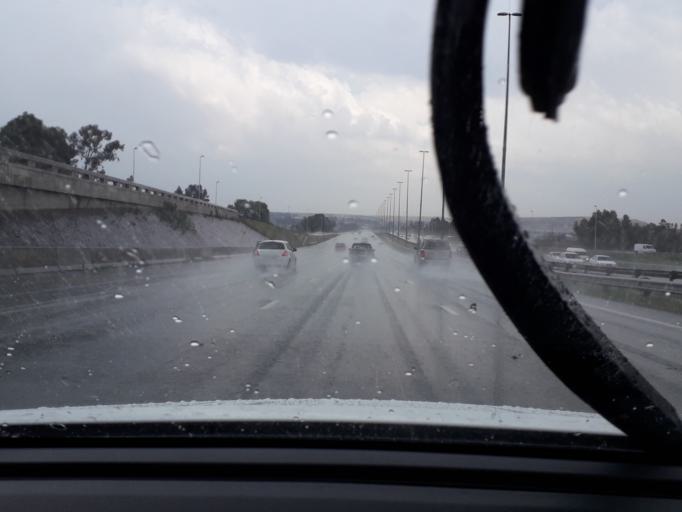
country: ZA
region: Gauteng
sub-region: City of Johannesburg Metropolitan Municipality
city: Roodepoort
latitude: -26.1868
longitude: 27.9469
